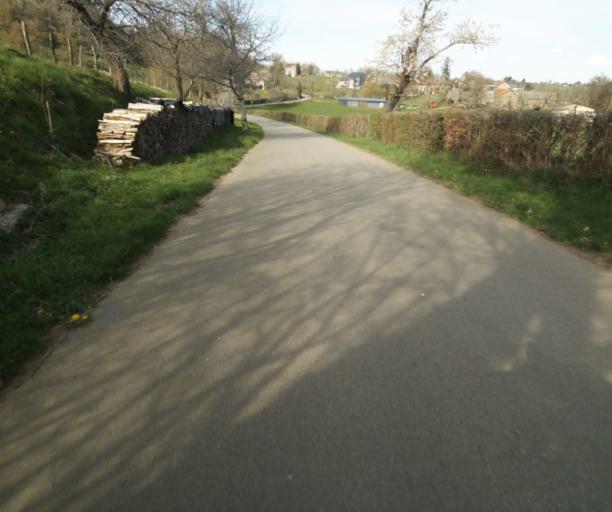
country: FR
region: Limousin
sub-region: Departement de la Correze
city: Naves
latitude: 45.3267
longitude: 1.7314
